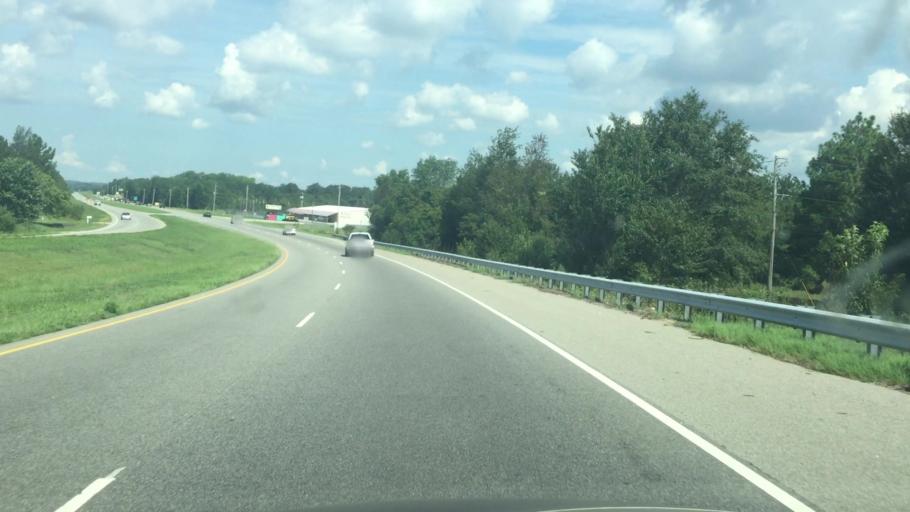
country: US
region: North Carolina
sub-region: Scotland County
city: Laurel Hill
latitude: 34.8353
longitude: -79.5960
